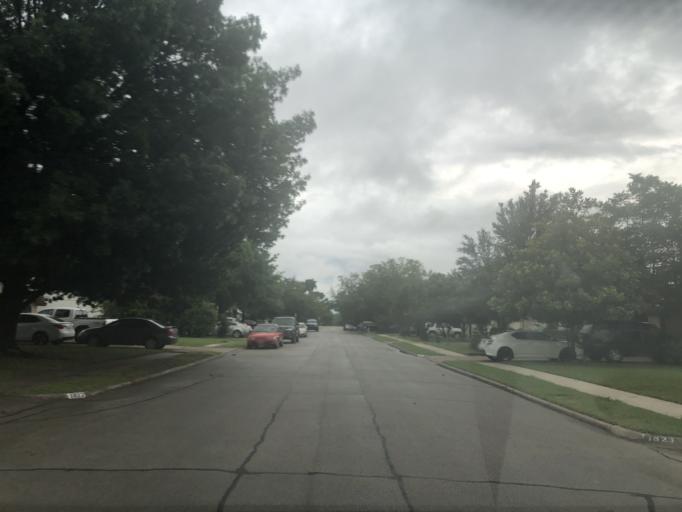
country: US
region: Texas
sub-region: Dallas County
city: Irving
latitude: 32.7956
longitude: -96.9507
